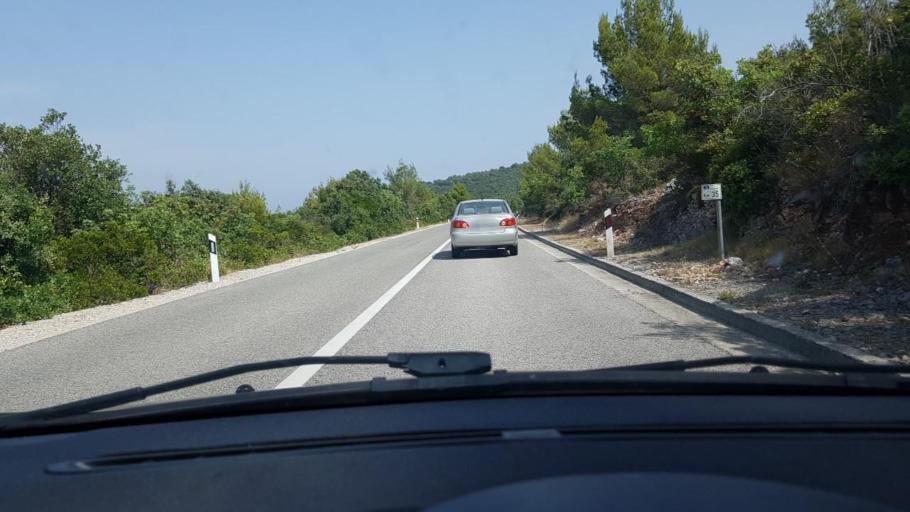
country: HR
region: Dubrovacko-Neretvanska
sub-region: Grad Korcula
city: Zrnovo
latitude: 42.9387
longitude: 17.0773
